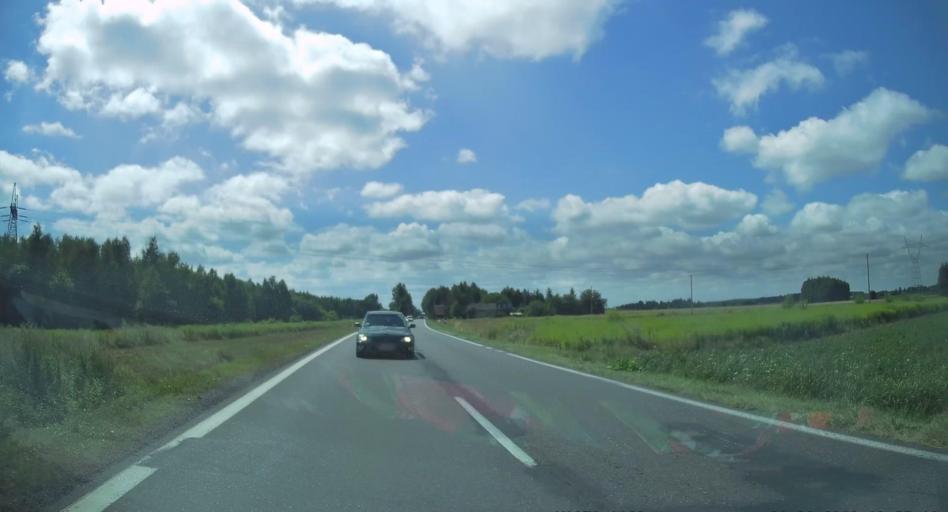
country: PL
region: Subcarpathian Voivodeship
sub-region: Powiat mielecki
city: Padew Narodowa
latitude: 50.4108
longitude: 21.4768
